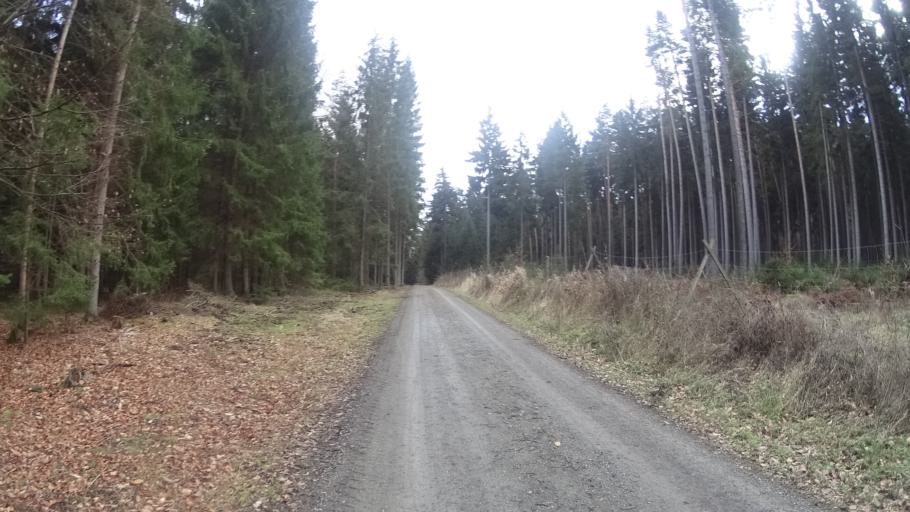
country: DE
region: Thuringia
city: Zeulenroda
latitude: 50.6258
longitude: 12.0139
